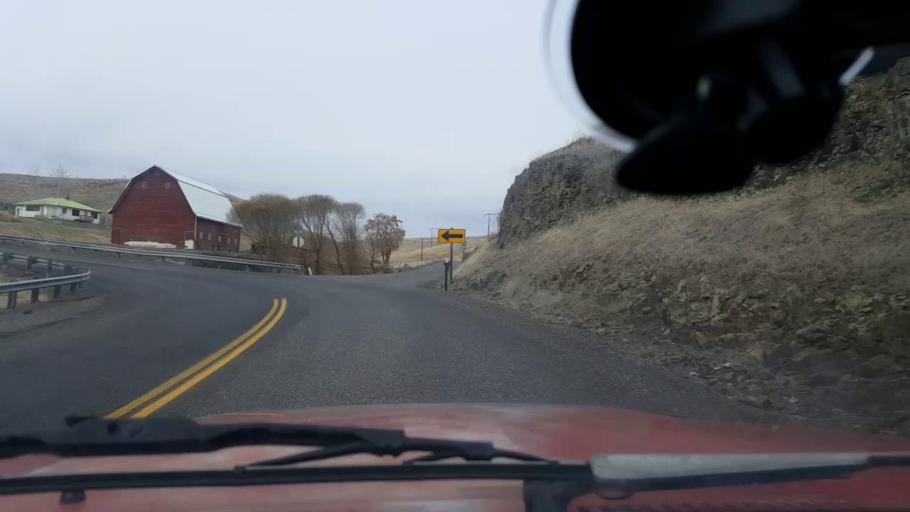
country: US
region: Washington
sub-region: Asotin County
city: Clarkston Heights-Vineland
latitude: 46.3861
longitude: -117.1383
